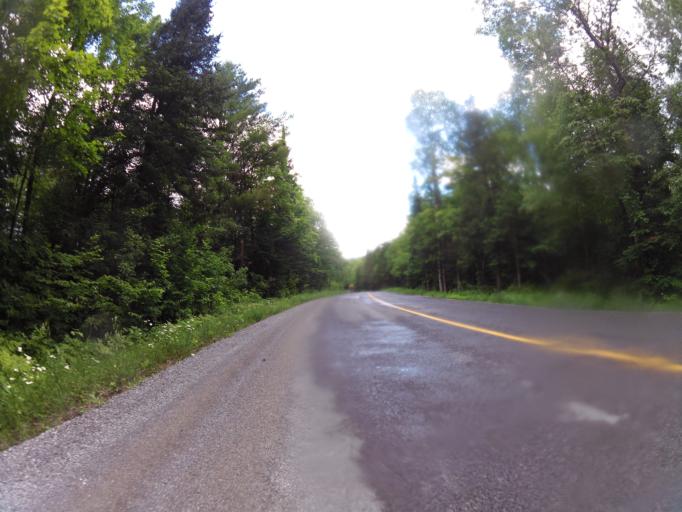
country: CA
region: Ontario
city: Renfrew
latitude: 45.0495
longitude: -76.6801
